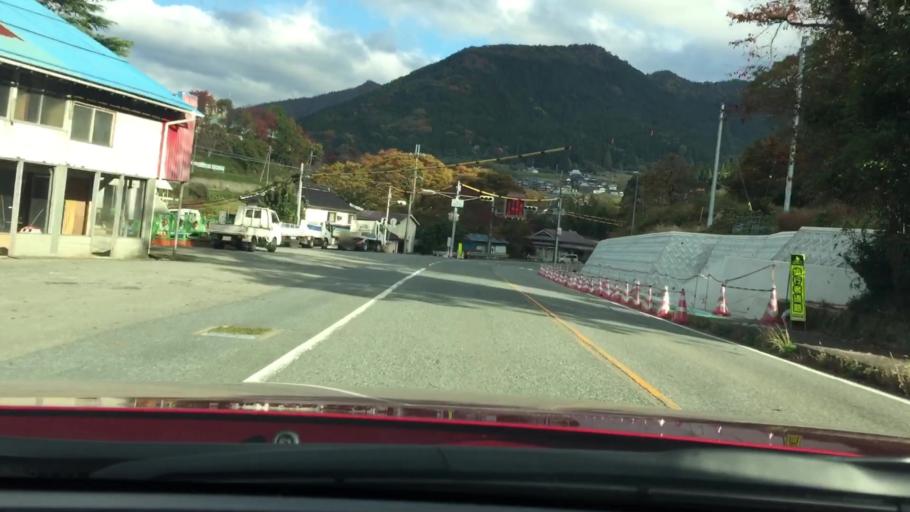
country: JP
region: Hyogo
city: Yamazakicho-nakabirose
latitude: 35.1690
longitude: 134.5440
